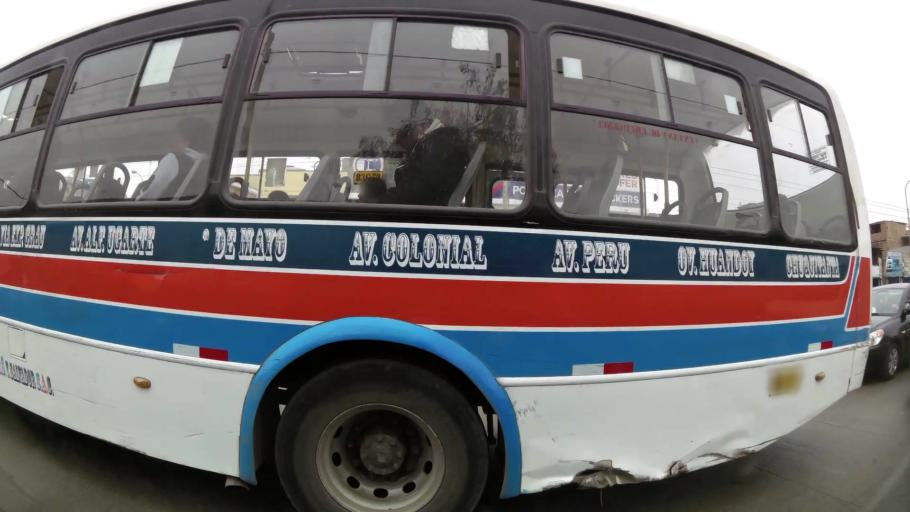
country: PE
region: Lima
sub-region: Lima
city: Surco
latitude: -12.1961
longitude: -76.9586
